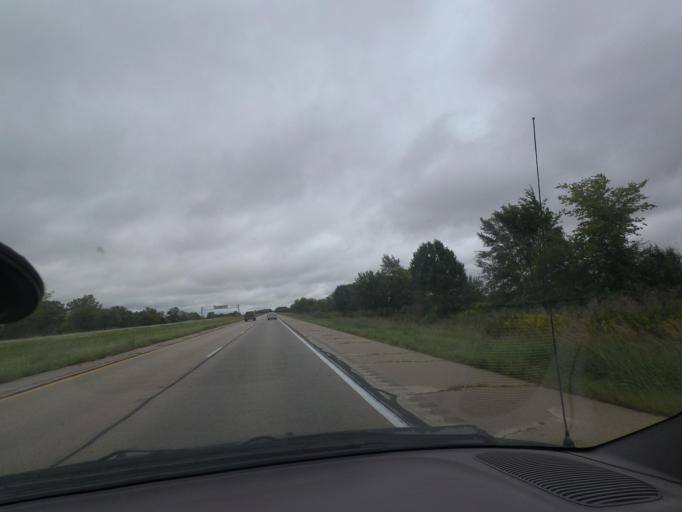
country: US
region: Illinois
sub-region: Piatt County
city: Cerro Gordo
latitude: 40.0182
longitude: -88.7246
